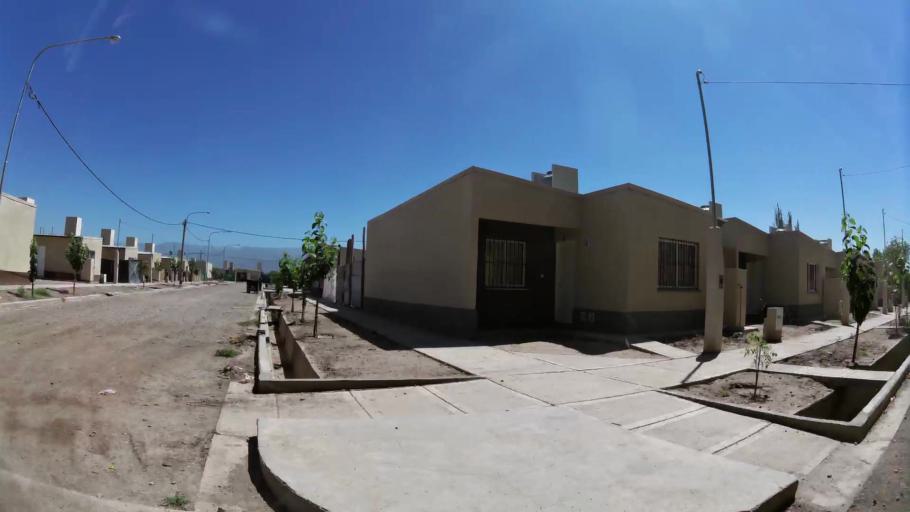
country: AR
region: Mendoza
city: Villa Nueva
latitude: -32.8747
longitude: -68.7876
